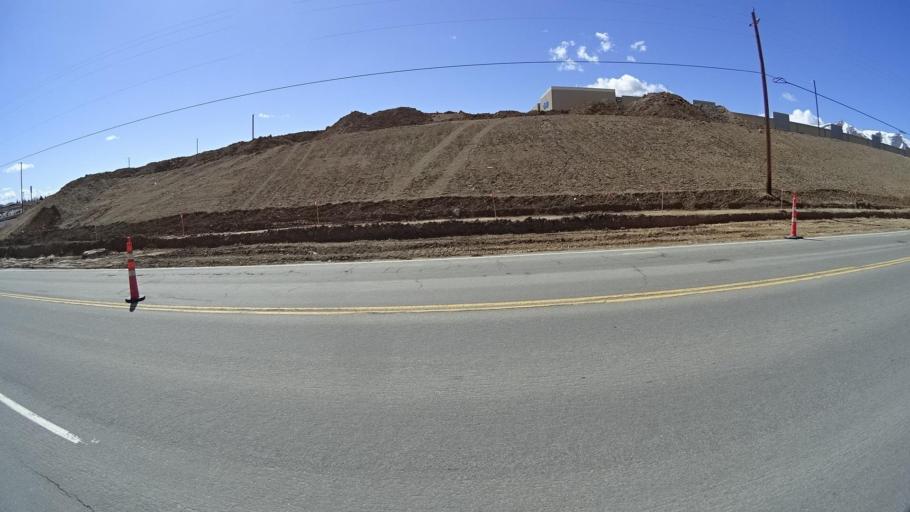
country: US
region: Nevada
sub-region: Washoe County
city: Golden Valley
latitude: 39.6019
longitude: -119.8480
